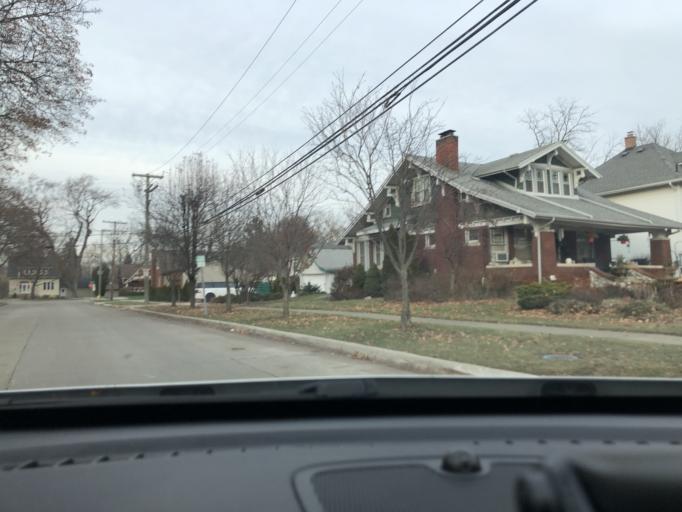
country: US
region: Michigan
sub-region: Wayne County
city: Dearborn Heights
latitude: 42.3053
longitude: -83.2540
